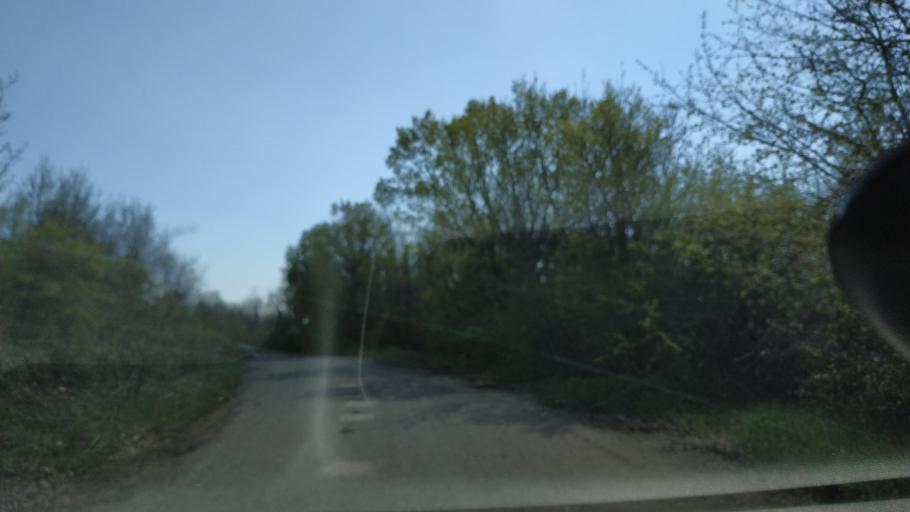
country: RS
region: Central Serbia
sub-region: Zajecarski Okrug
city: Soko Banja
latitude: 43.5587
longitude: 21.8933
